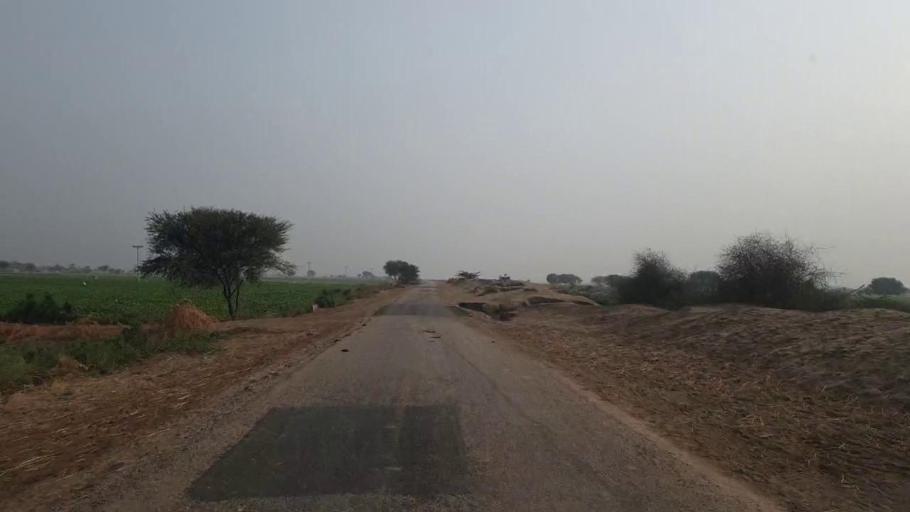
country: PK
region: Sindh
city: Mirpur Batoro
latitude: 24.5762
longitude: 68.3971
